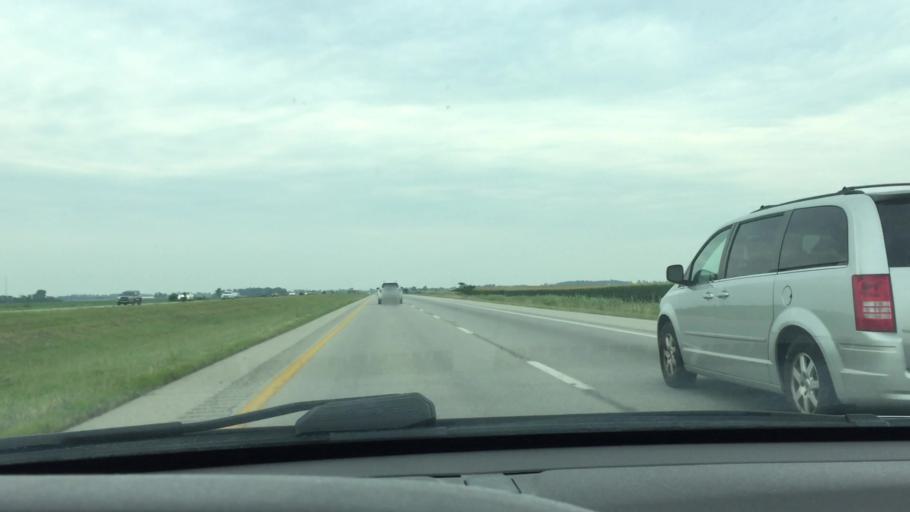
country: US
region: Ohio
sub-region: Clinton County
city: Wilmington
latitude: 39.5403
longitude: -83.7700
